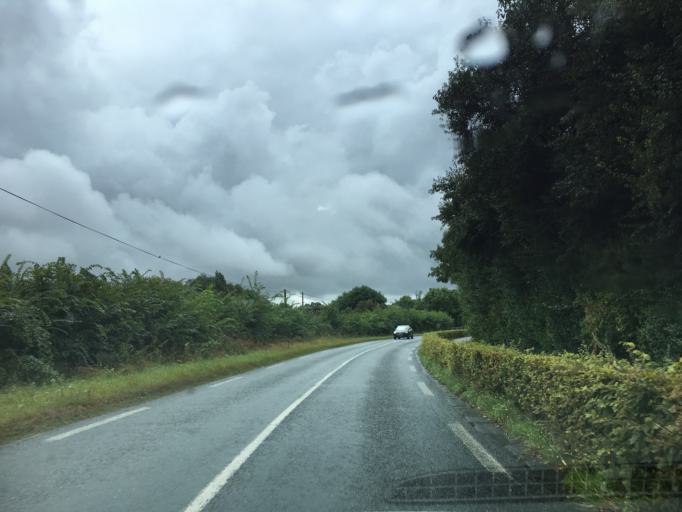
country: FR
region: Lower Normandy
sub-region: Departement du Calvados
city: Amfreville
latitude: 49.2667
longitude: -0.2214
